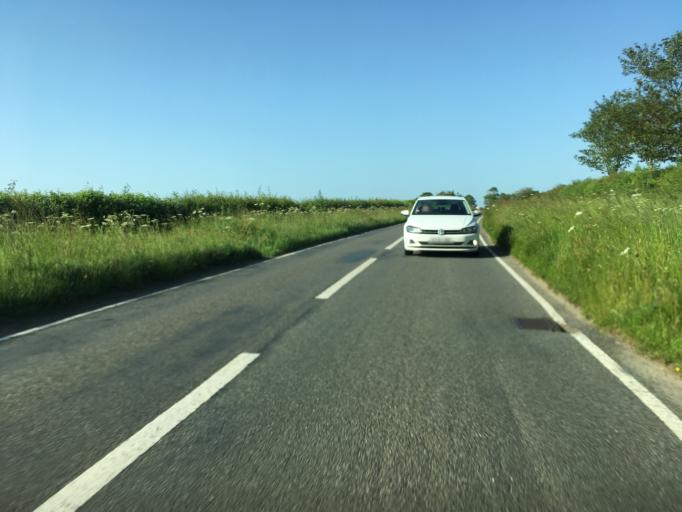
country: GB
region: England
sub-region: Oxfordshire
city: Charlbury
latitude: 51.8892
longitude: -1.4724
